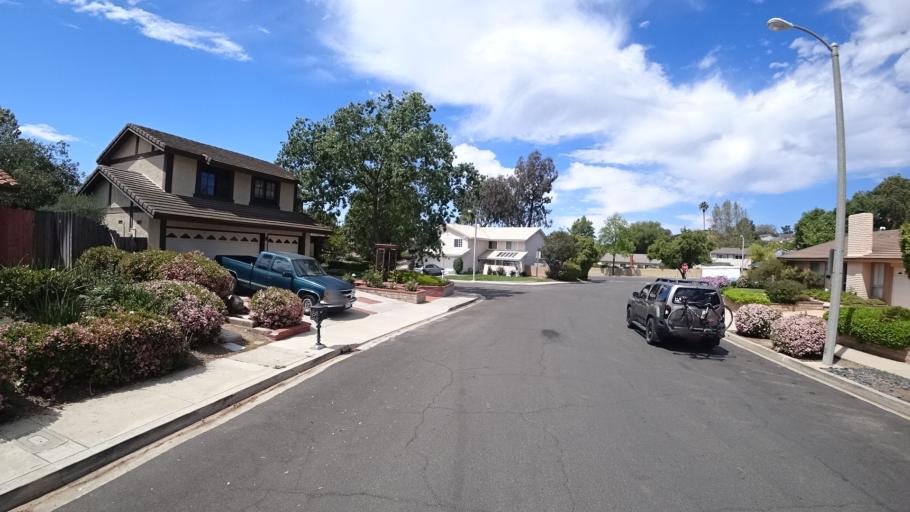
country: US
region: California
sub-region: Ventura County
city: Casa Conejo
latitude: 34.1647
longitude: -118.9419
